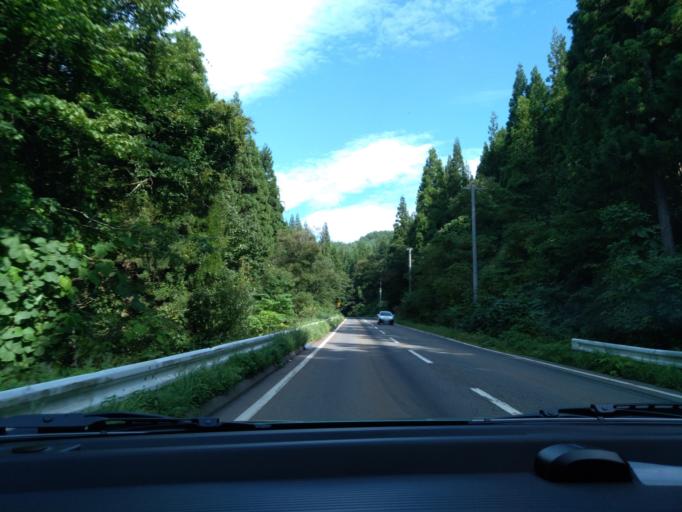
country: JP
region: Iwate
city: Shizukuishi
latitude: 39.6385
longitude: 141.0085
